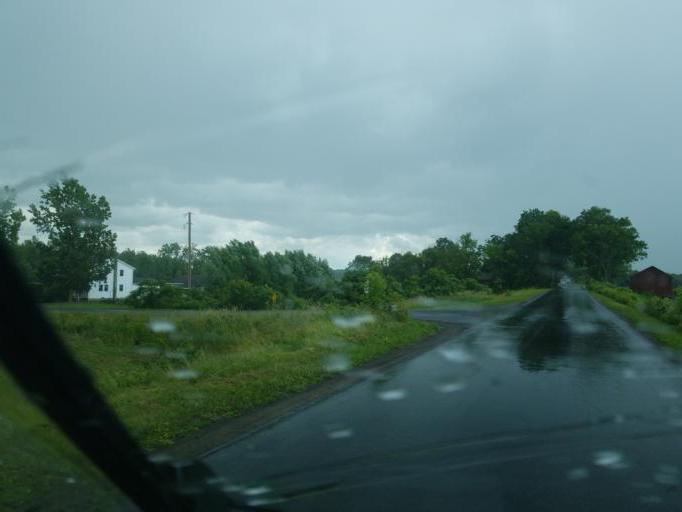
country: US
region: New York
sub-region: Wayne County
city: Clyde
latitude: 43.0196
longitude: -76.8791
